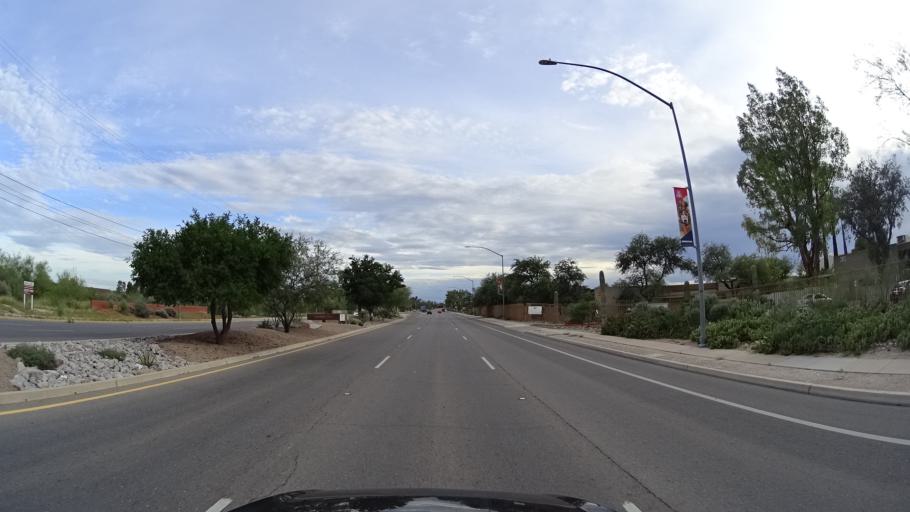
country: US
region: Arizona
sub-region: Pima County
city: Summit
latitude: 32.1301
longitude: -110.9347
